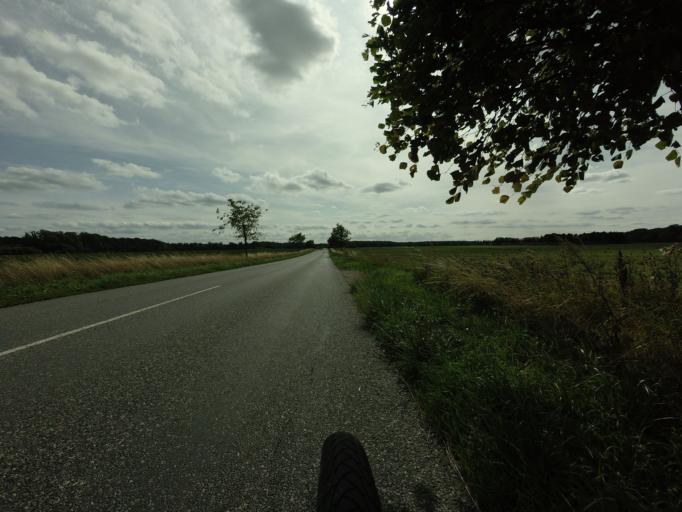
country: DK
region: Zealand
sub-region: Faxe Kommune
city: Fakse Ladeplads
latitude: 55.2489
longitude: 12.2215
